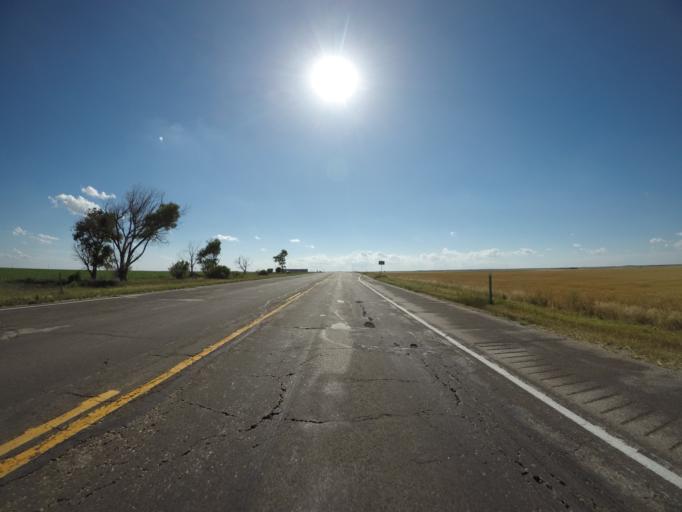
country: US
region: Colorado
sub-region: Logan County
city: Sterling
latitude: 40.6239
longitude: -103.3500
